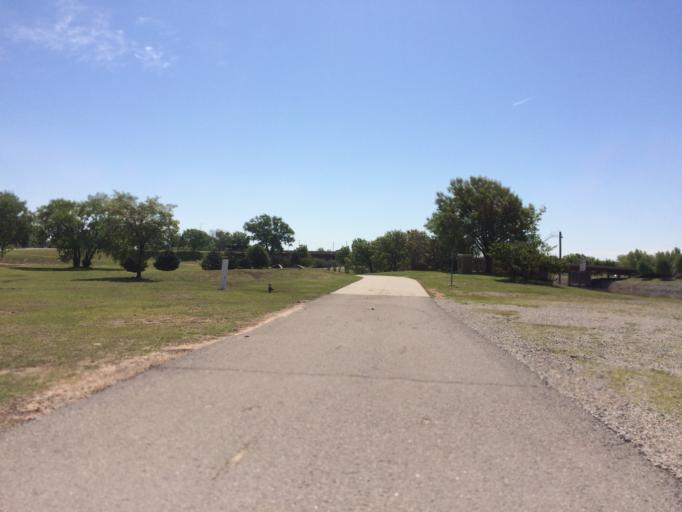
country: US
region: Oklahoma
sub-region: Oklahoma County
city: Oklahoma City
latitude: 35.4502
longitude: -97.5240
